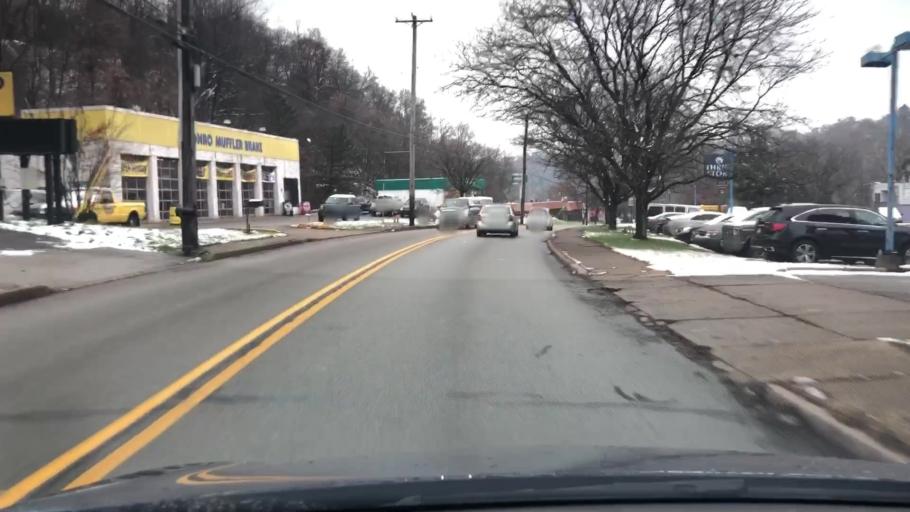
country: US
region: Pennsylvania
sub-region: Allegheny County
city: Churchill
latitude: 40.4545
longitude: -79.8234
